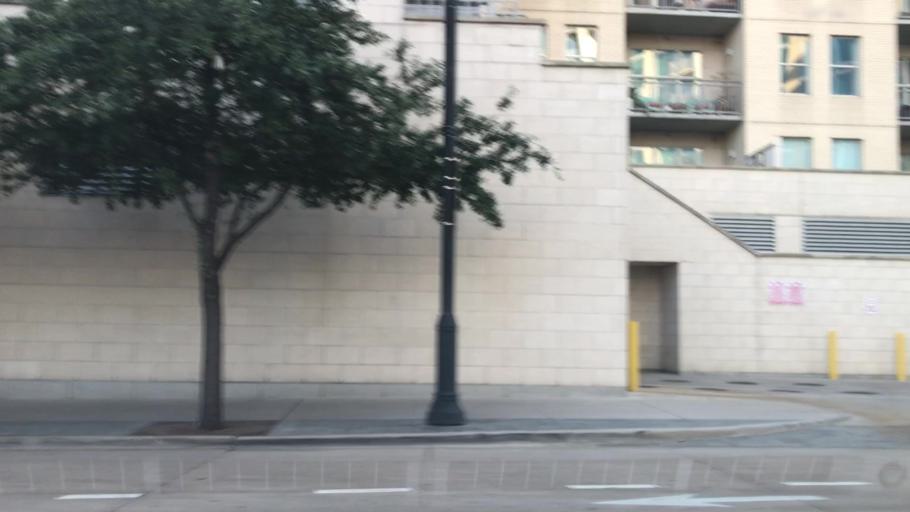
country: US
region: Texas
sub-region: Dallas County
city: Dallas
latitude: 32.7857
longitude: -96.8088
